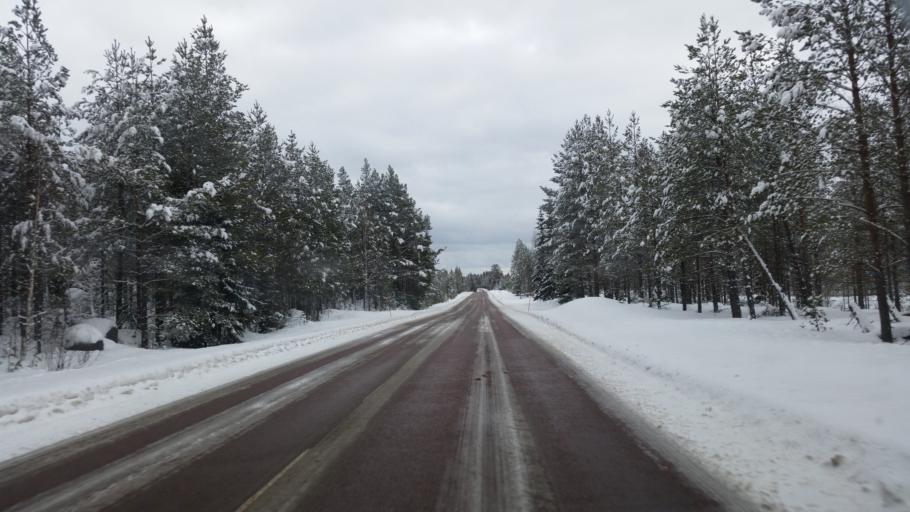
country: SE
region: Jaemtland
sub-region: Harjedalens Kommun
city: Sveg
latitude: 62.1864
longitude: 14.8666
